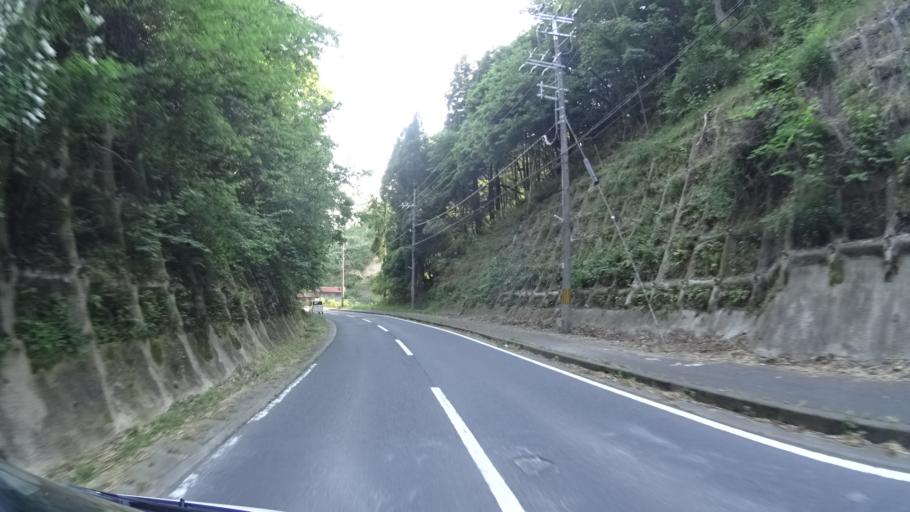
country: JP
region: Kyoto
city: Miyazu
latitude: 35.5635
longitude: 135.1418
